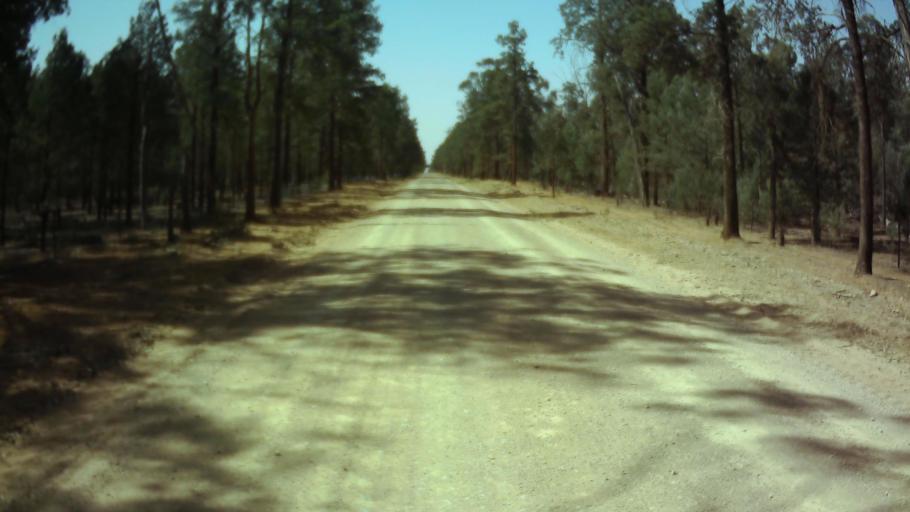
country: AU
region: New South Wales
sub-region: Weddin
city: Grenfell
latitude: -33.9707
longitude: 147.9304
